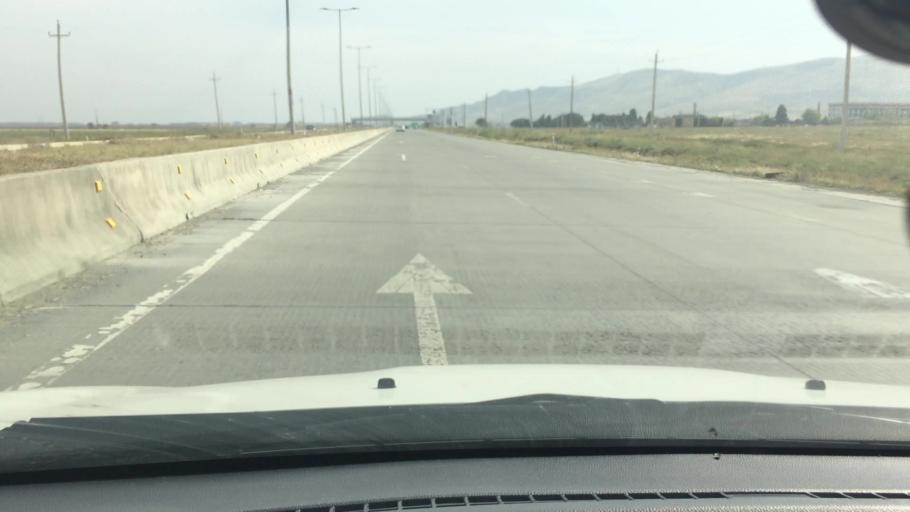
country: GE
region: Kvemo Kartli
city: Rust'avi
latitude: 41.5981
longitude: 44.9423
